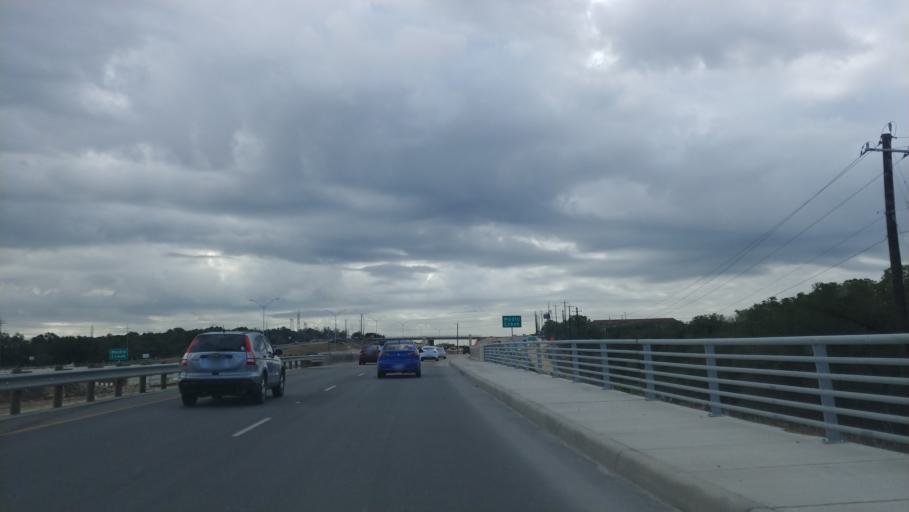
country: US
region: Texas
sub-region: Bexar County
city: Lackland Air Force Base
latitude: 29.4217
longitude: -98.7105
